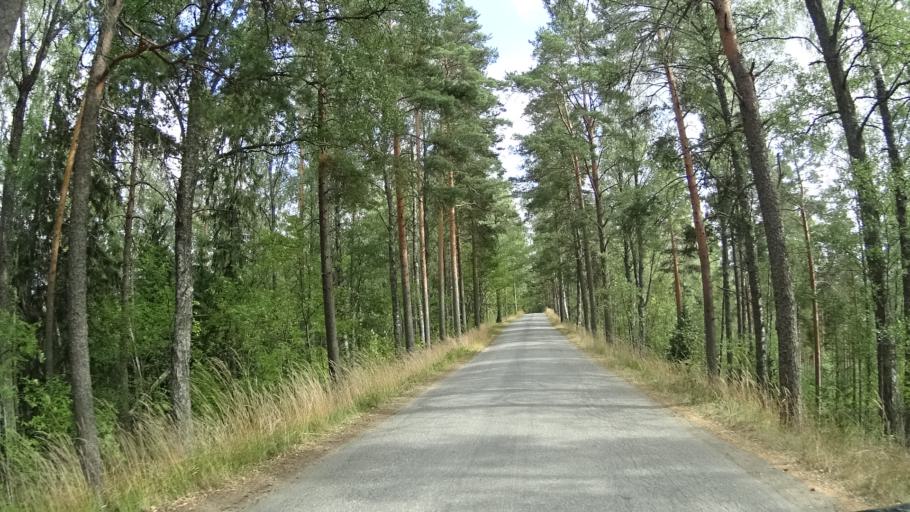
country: FI
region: Pirkanmaa
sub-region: Tampere
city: Kangasala
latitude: 61.4078
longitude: 24.1591
